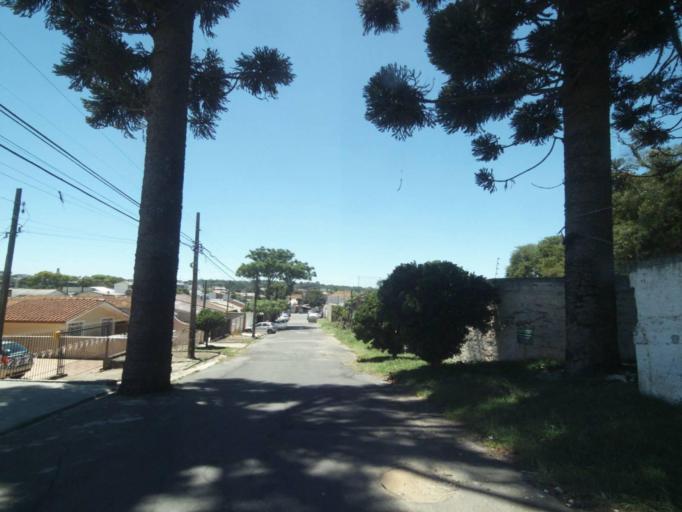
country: BR
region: Parana
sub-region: Curitiba
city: Curitiba
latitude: -25.4765
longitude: -49.3462
